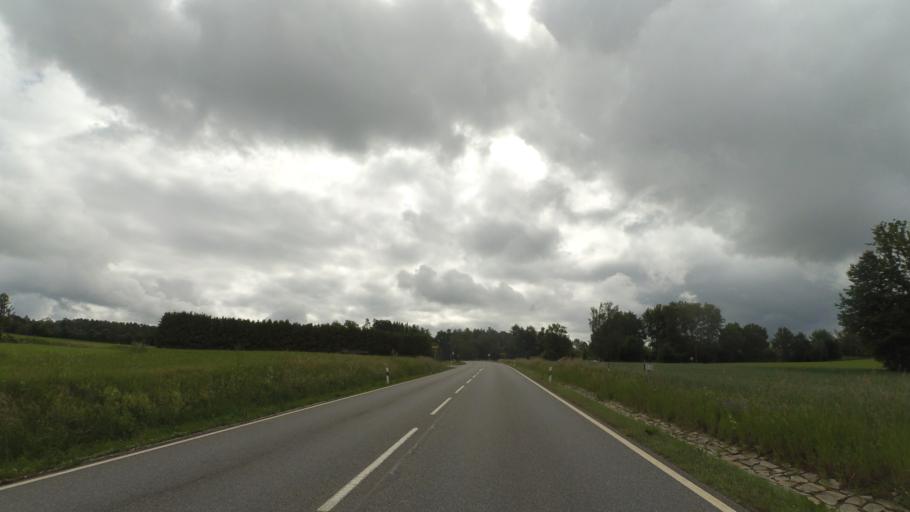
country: DE
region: Bavaria
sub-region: Lower Bavaria
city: Prackenbach
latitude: 49.0890
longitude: 12.8399
